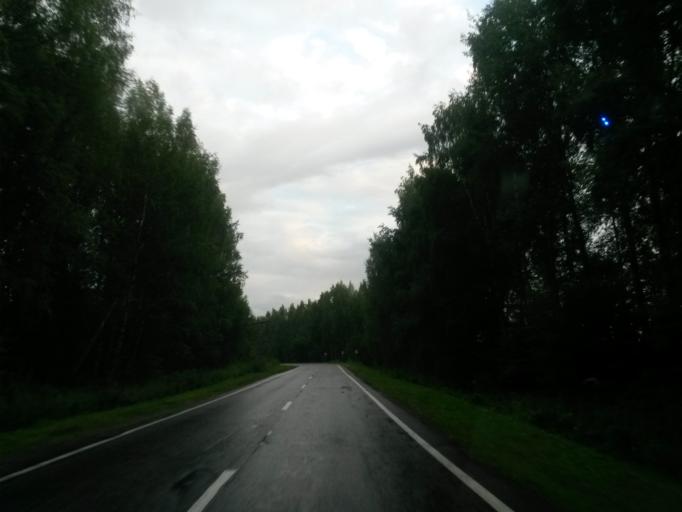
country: RU
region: Jaroslavl
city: Tutayev
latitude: 57.9149
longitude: 39.5155
